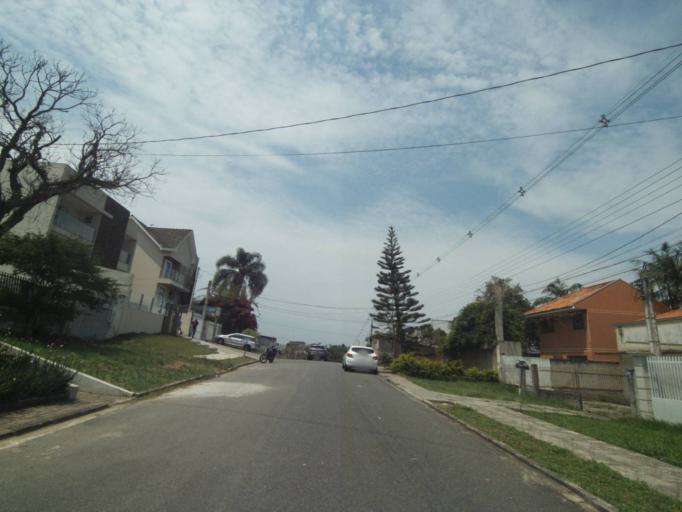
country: BR
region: Parana
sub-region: Pinhais
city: Pinhais
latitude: -25.4191
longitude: -49.2097
